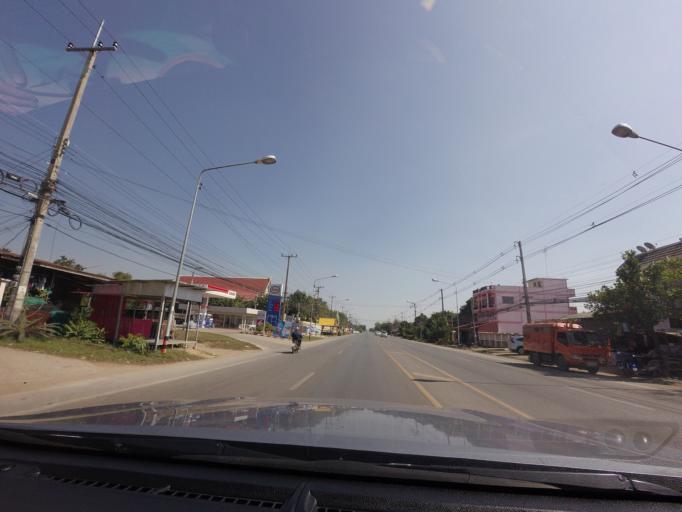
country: TH
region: Sukhothai
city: Sukhothai
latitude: 17.0112
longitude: 99.7809
